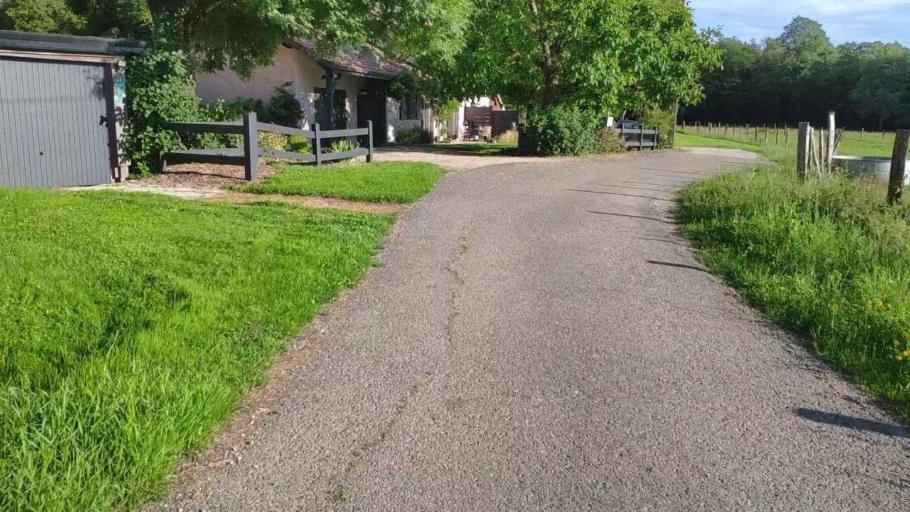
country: FR
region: Franche-Comte
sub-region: Departement du Jura
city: Bletterans
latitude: 46.7799
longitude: 5.4812
